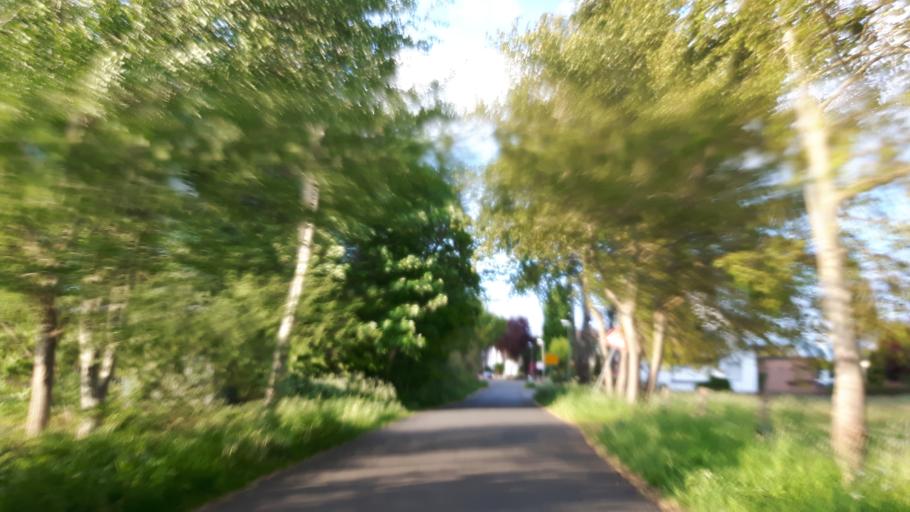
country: DE
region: Lower Saxony
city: Delmenhorst
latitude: 53.0313
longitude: 8.6151
